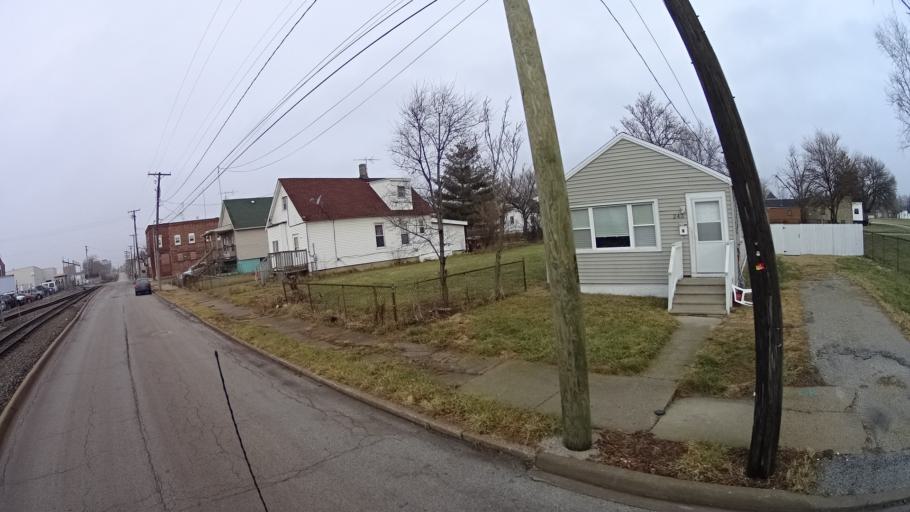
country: US
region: Illinois
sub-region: Cook County
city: Chicago Heights
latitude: 41.5008
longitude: -87.6262
